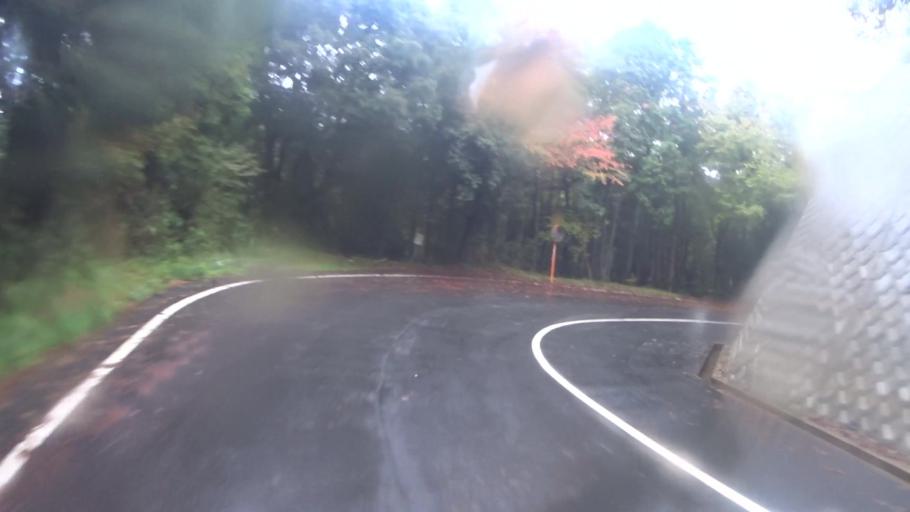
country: JP
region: Kyoto
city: Miyazu
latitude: 35.5249
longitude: 135.2344
